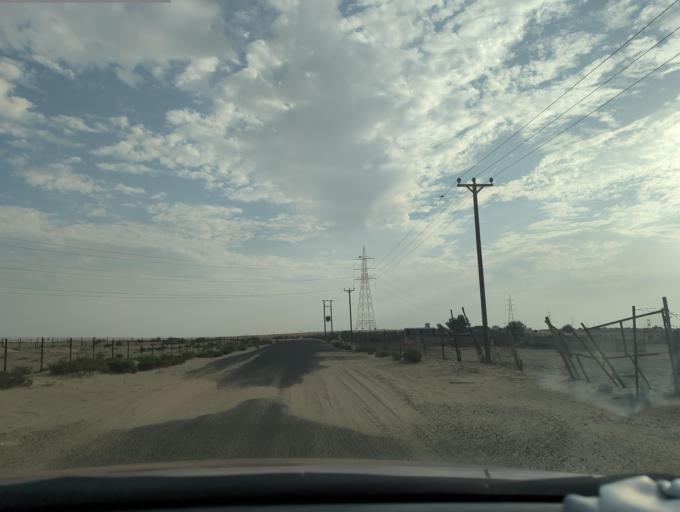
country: AE
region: Dubai
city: Dubai
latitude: 24.7142
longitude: 54.8717
